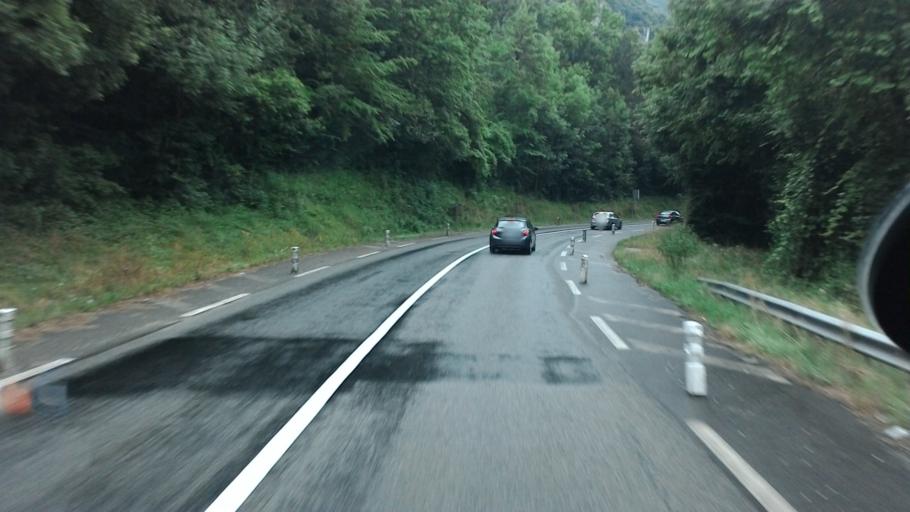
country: FR
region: Rhone-Alpes
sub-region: Departement de la Savoie
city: Le Bourget-du-Lac
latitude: 45.6926
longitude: 5.8294
